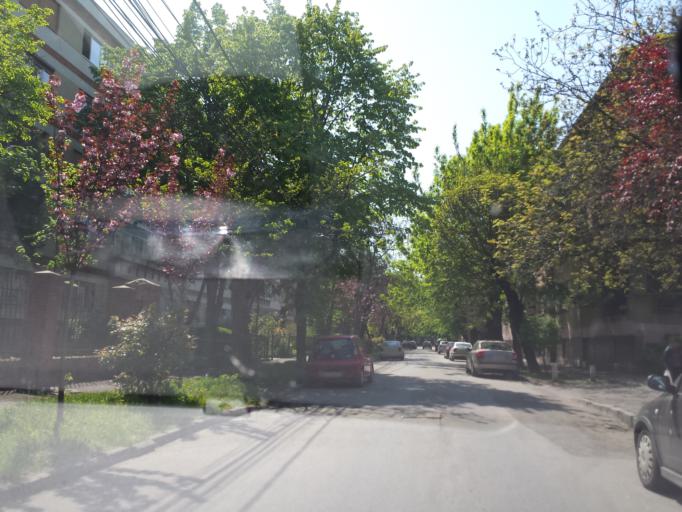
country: RO
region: Timis
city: Timisoara
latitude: 45.7570
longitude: 21.2353
